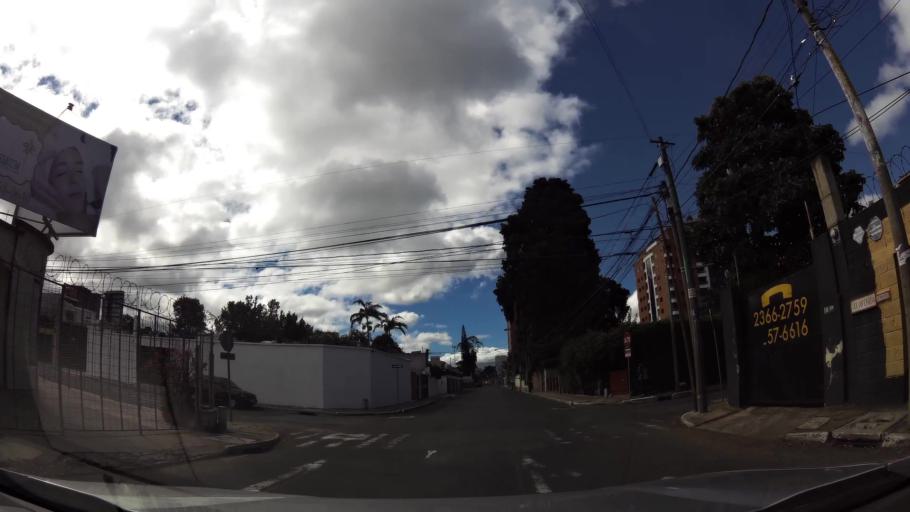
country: GT
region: Guatemala
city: Santa Catarina Pinula
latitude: 14.5945
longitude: -90.5069
